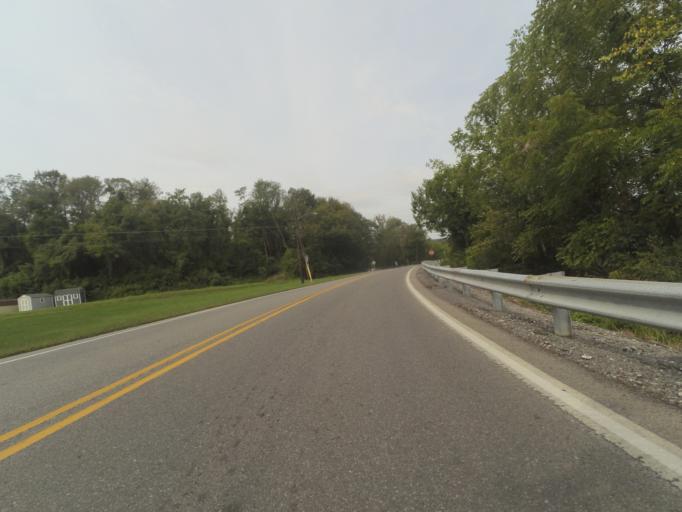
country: US
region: Pennsylvania
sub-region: Huntingdon County
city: McConnellstown
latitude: 40.5503
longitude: -78.0999
